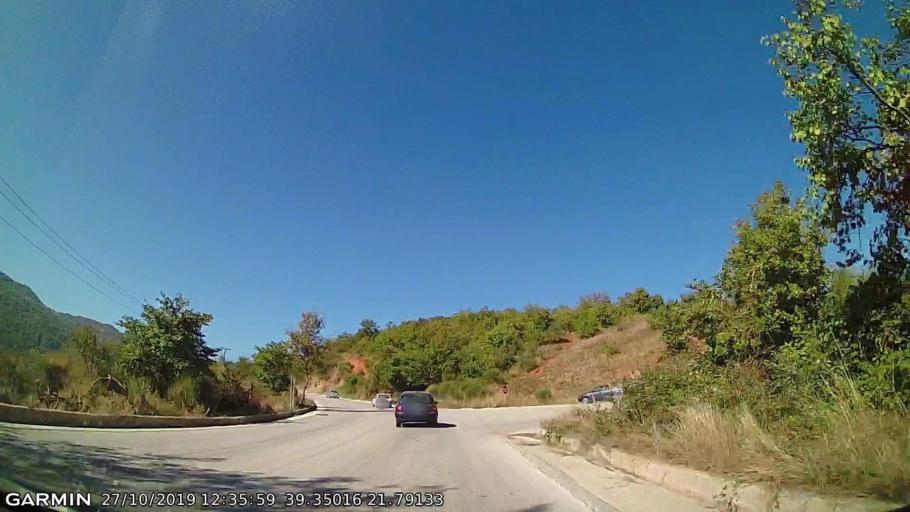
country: GR
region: Thessaly
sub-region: Nomos Kardhitsas
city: Morfovouni
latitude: 39.3502
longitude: 21.7913
